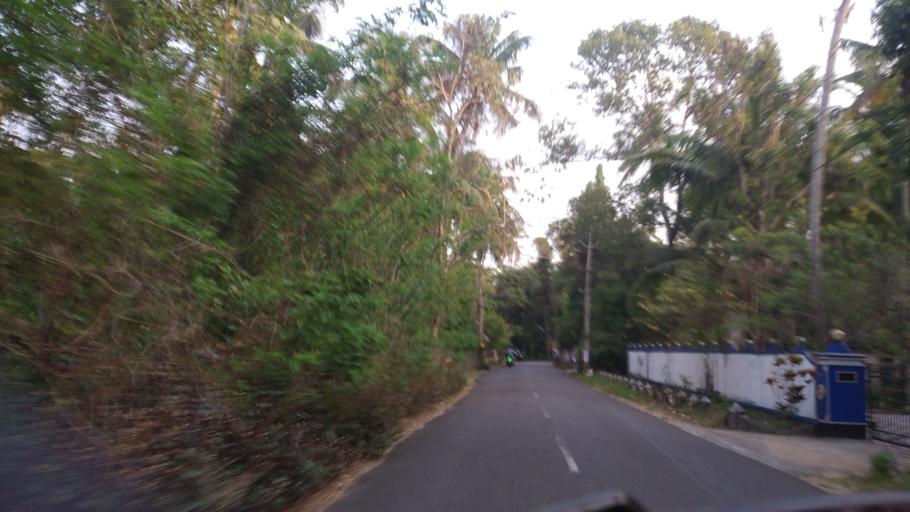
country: IN
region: Kerala
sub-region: Thrissur District
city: Thanniyam
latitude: 10.3475
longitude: 76.1141
